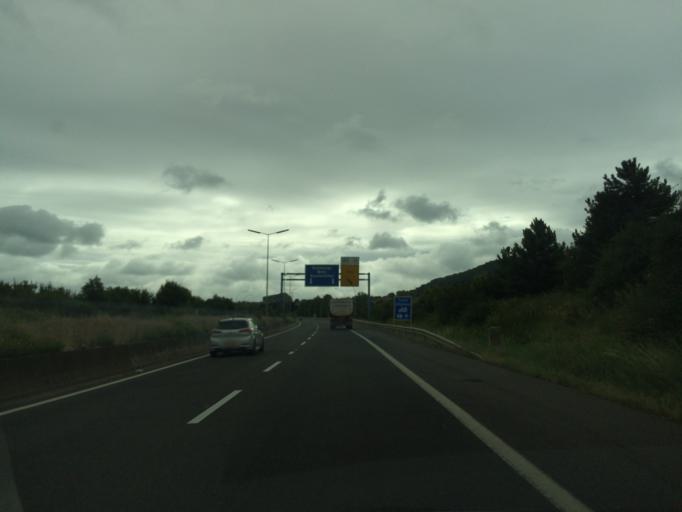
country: LU
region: Luxembourg
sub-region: Canton d'Esch-sur-Alzette
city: Kayl
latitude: 49.5019
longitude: 6.0455
